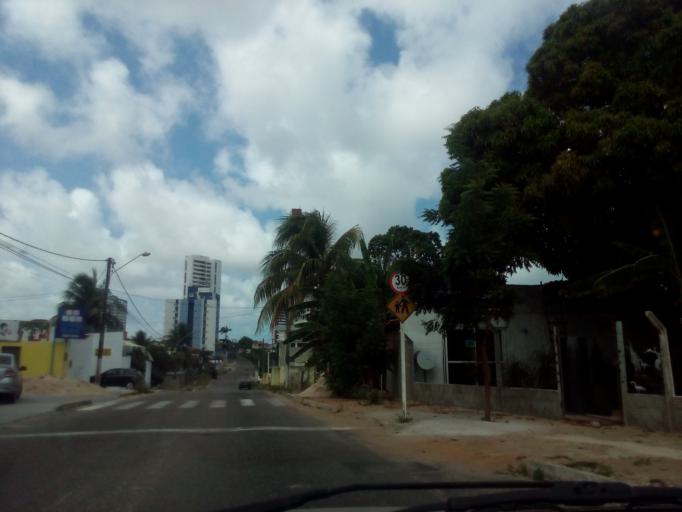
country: BR
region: Rio Grande do Norte
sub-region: Natal
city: Natal
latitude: -5.8593
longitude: -35.2048
